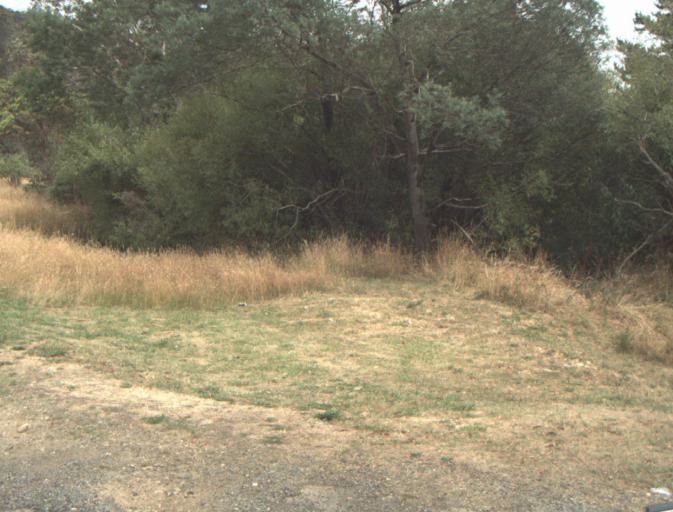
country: AU
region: Tasmania
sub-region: Northern Midlands
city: Evandale
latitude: -41.4963
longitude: 147.4200
